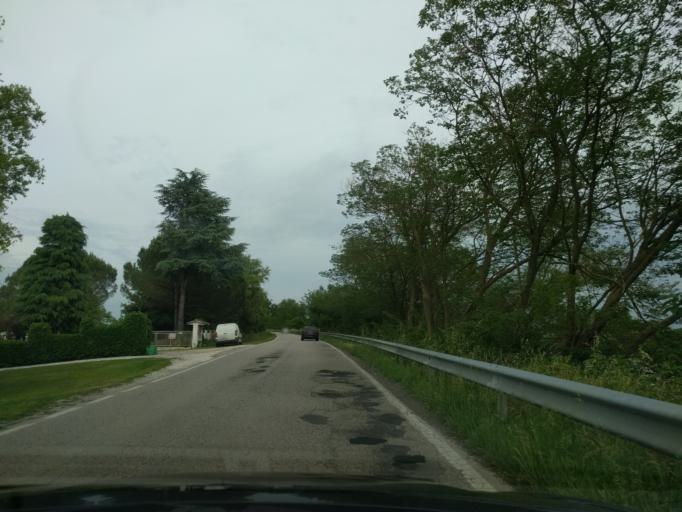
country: IT
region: Veneto
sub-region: Provincia di Rovigo
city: Gavello
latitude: 45.0308
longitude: 11.9348
